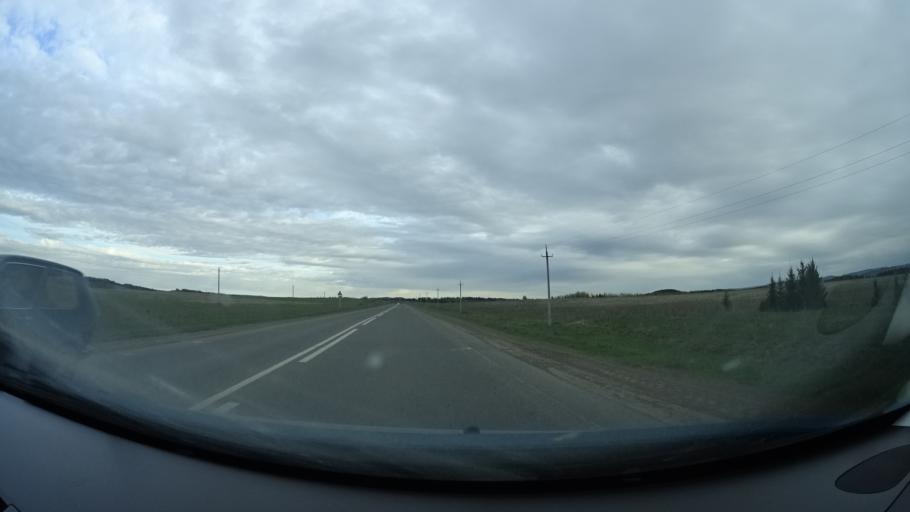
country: RU
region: Perm
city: Osa
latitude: 57.2468
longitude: 55.5908
